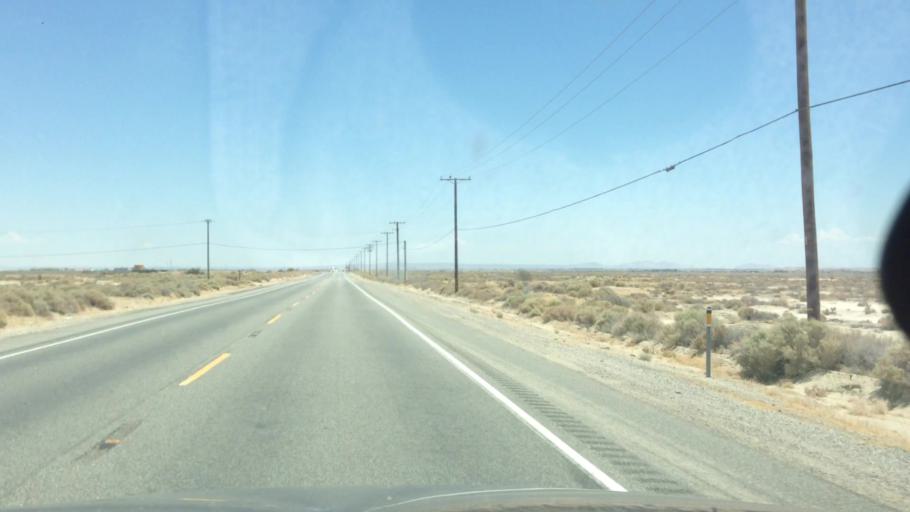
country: US
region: California
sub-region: Kern County
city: Rosamond
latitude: 34.7767
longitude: -118.1957
